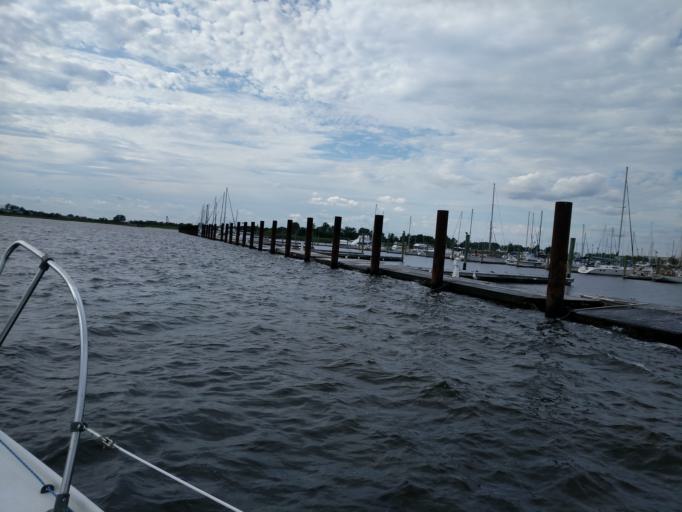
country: US
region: New York
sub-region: Kings County
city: Brooklyn
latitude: 40.5832
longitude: -73.9011
